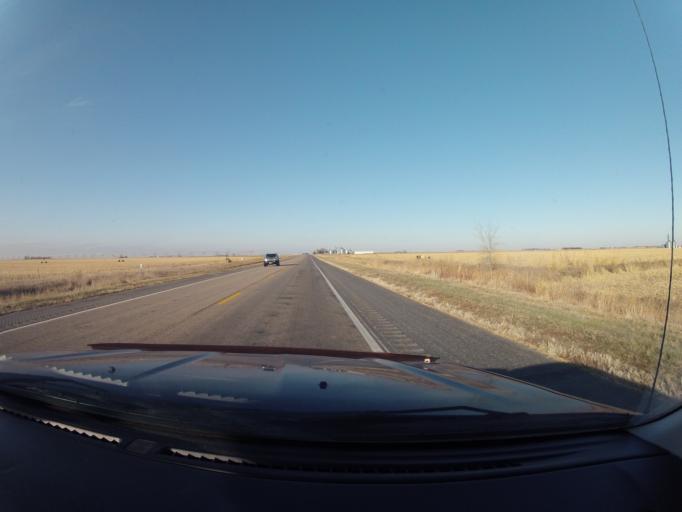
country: US
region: Nebraska
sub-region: Kearney County
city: Minden
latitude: 40.5197
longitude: -98.9518
